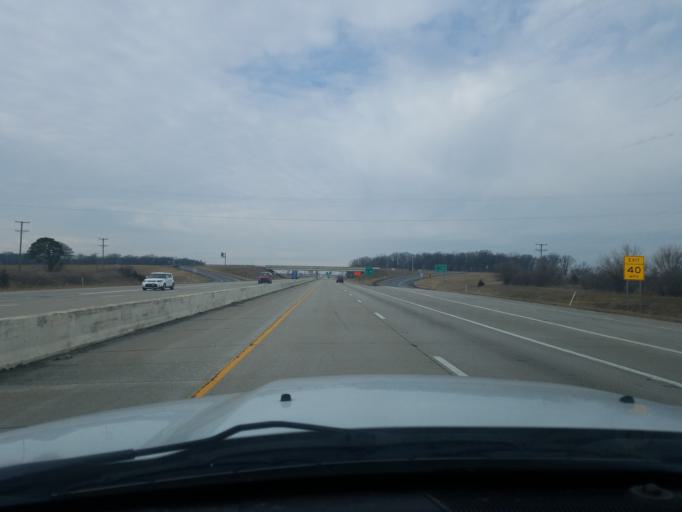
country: US
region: Indiana
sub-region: Wells County
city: Ossian
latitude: 40.9532
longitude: -85.2546
